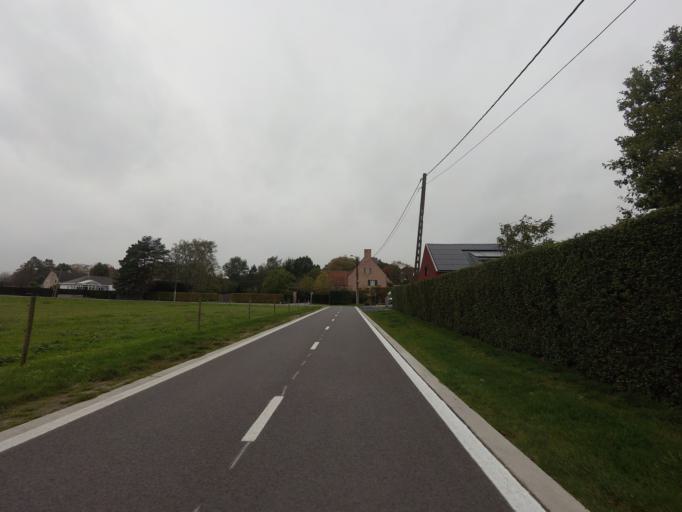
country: BE
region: Flanders
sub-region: Provincie Antwerpen
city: Bonheiden
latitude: 51.0241
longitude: 4.5265
